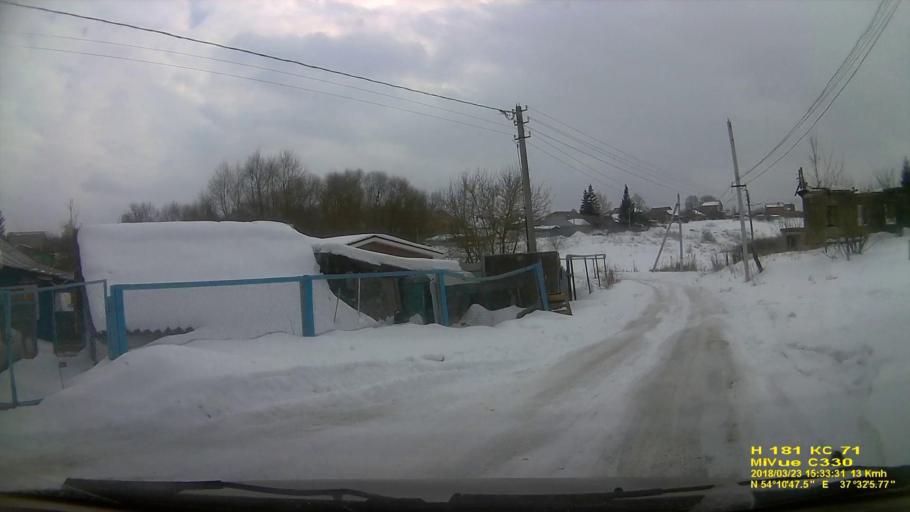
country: RU
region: Tula
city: Kosaya Gora
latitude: 54.1799
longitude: 37.5349
